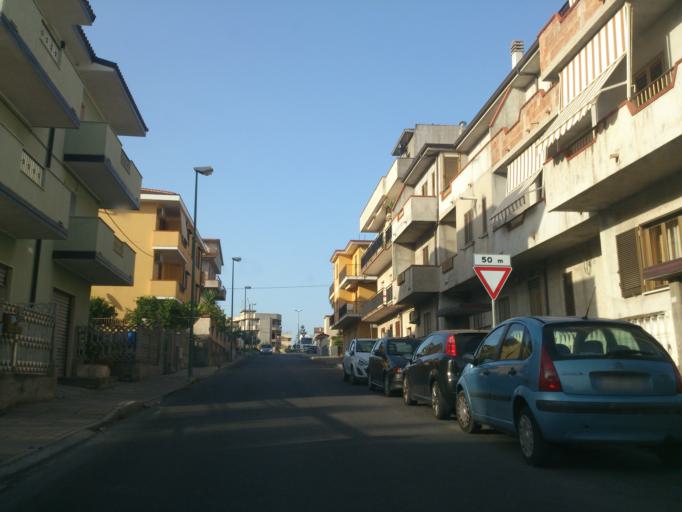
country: IT
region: Calabria
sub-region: Provincia di Reggio Calabria
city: Monasterace Marina
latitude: 38.4356
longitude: 16.5711
